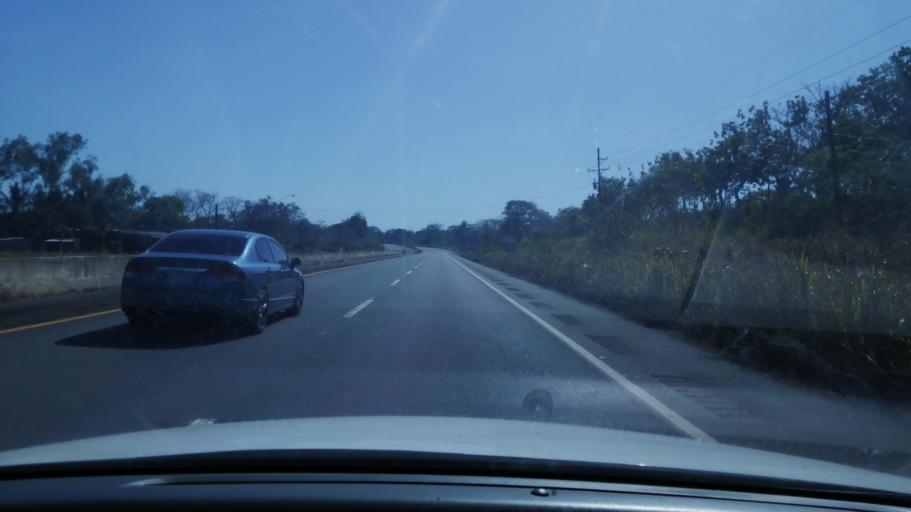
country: PA
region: Chiriqui
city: San Felix
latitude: 8.2778
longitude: -81.9598
